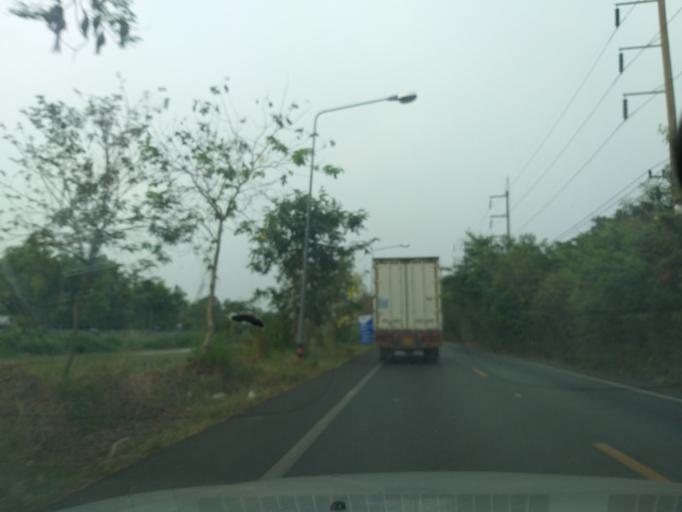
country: TH
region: Pathum Thani
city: Ban Lam Luk Ka
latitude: 13.9748
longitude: 100.8958
